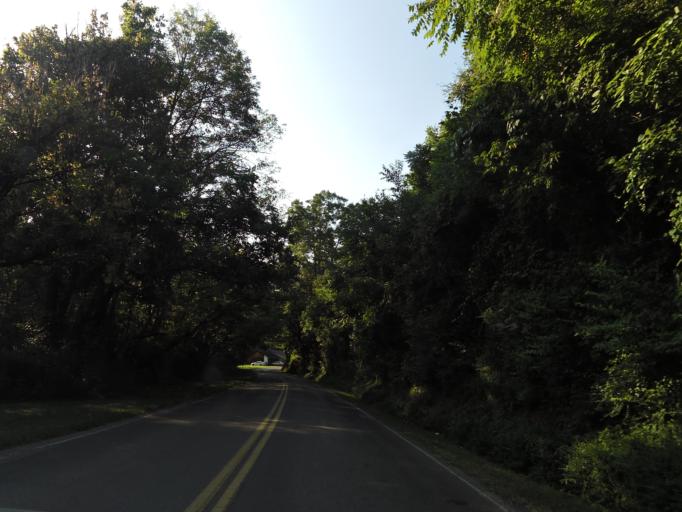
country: US
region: Tennessee
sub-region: Blount County
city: Eagleton Village
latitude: 35.8164
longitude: -83.9419
